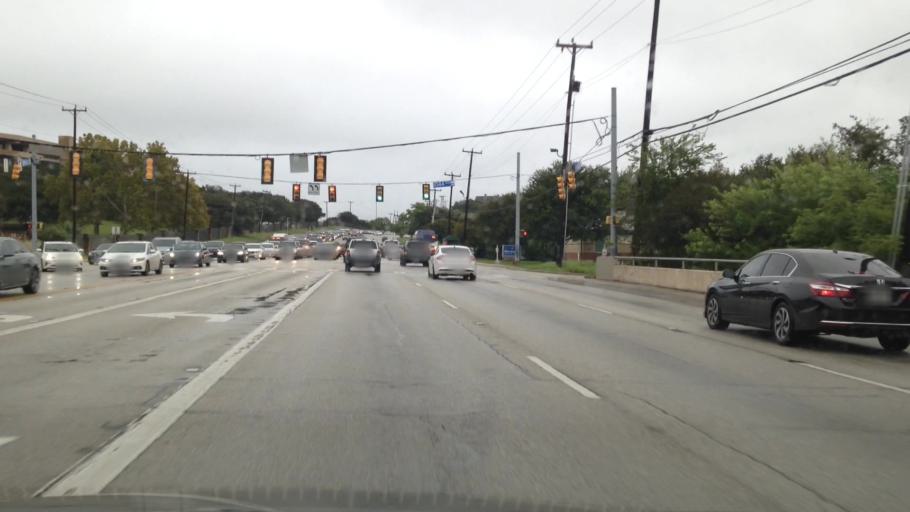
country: US
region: Texas
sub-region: Bexar County
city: Shavano Park
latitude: 29.5380
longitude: -98.5786
